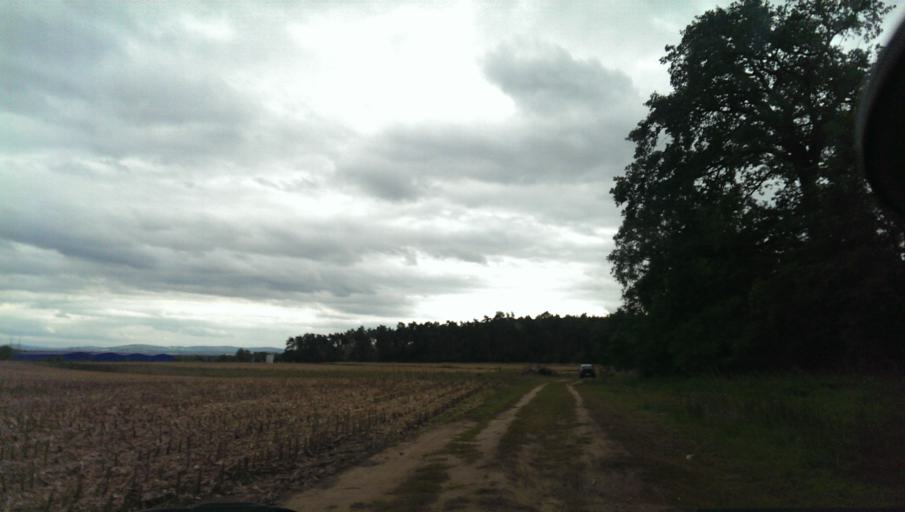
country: CZ
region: South Moravian
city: Moravsky Pisek
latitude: 48.9908
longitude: 17.3147
